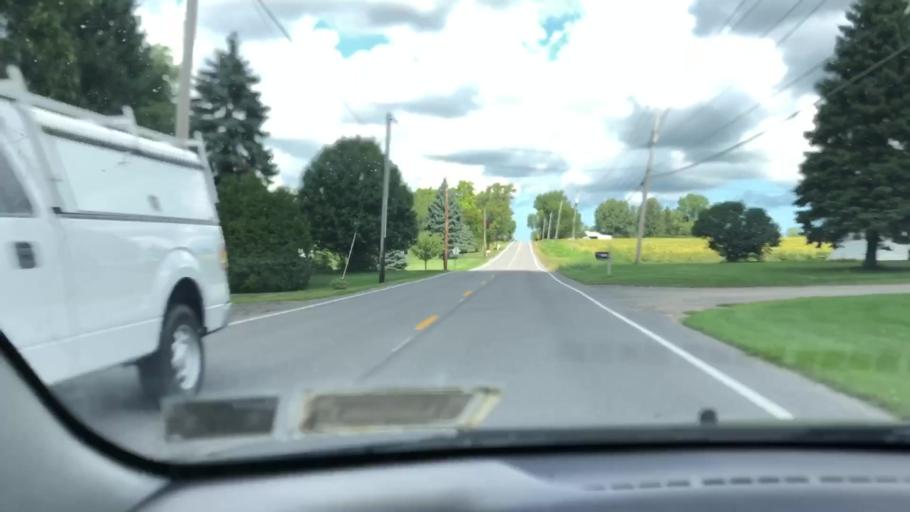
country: US
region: New York
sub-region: Wayne County
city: Macedon
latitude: 43.1045
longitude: -77.3207
